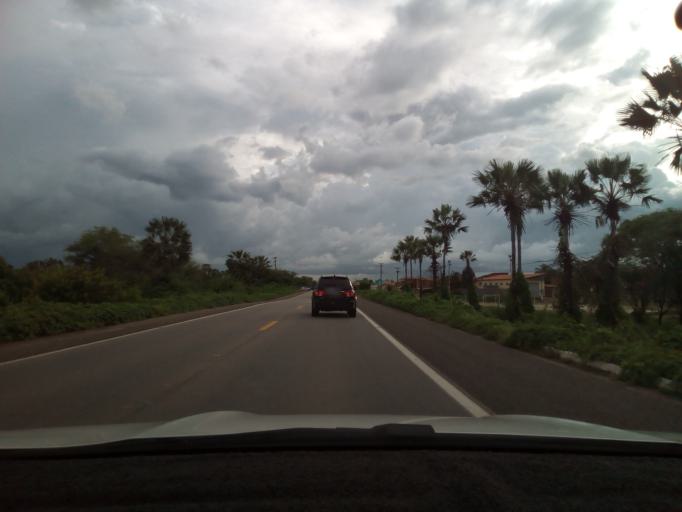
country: BR
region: Ceara
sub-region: Aracati
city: Aracati
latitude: -4.5723
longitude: -37.7599
